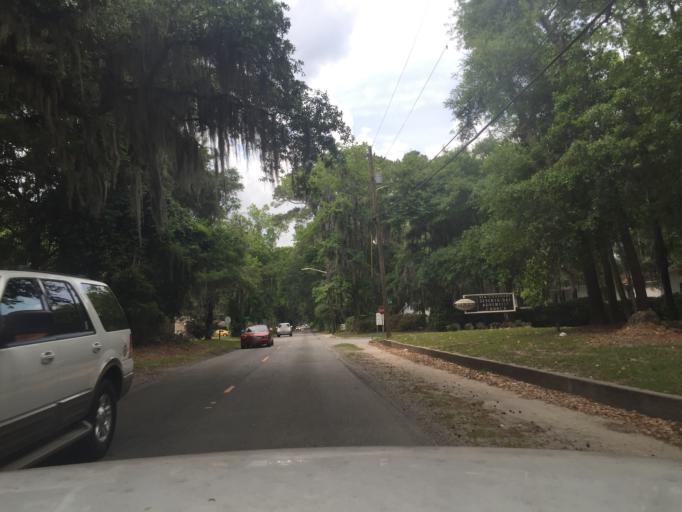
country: US
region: Georgia
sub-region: Chatham County
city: Thunderbolt
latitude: 32.0195
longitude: -81.0676
